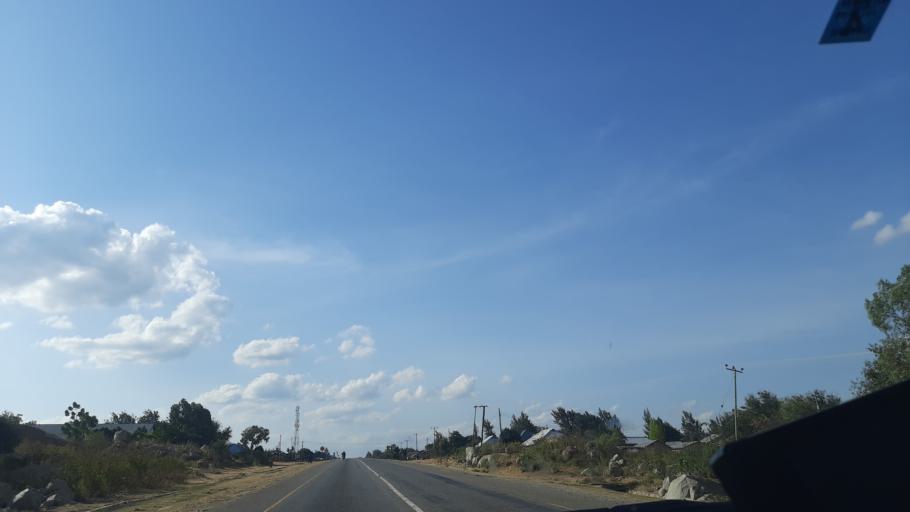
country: TZ
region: Singida
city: Puma
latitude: -5.0088
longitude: 34.7574
